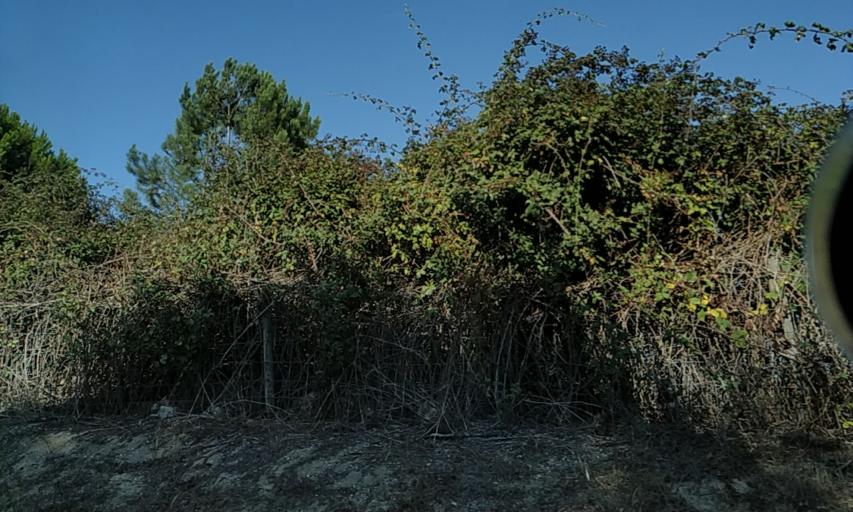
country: PT
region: Evora
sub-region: Vendas Novas
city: Vendas Novas
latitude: 38.7214
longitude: -8.6196
